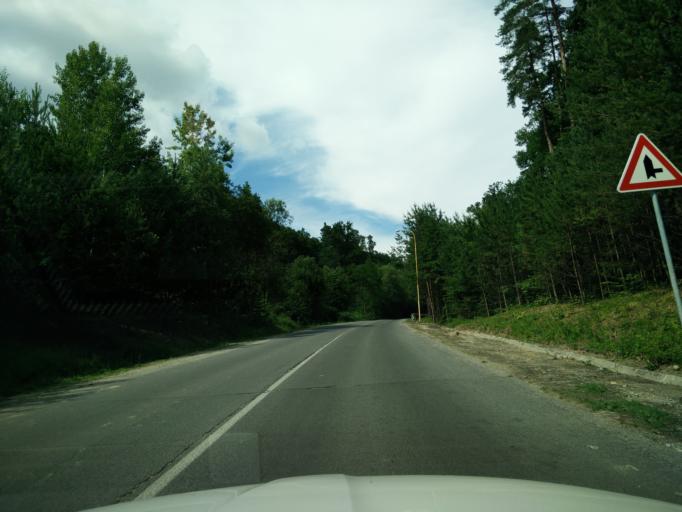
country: SK
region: Nitriansky
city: Bojnice
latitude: 48.8074
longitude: 18.5784
